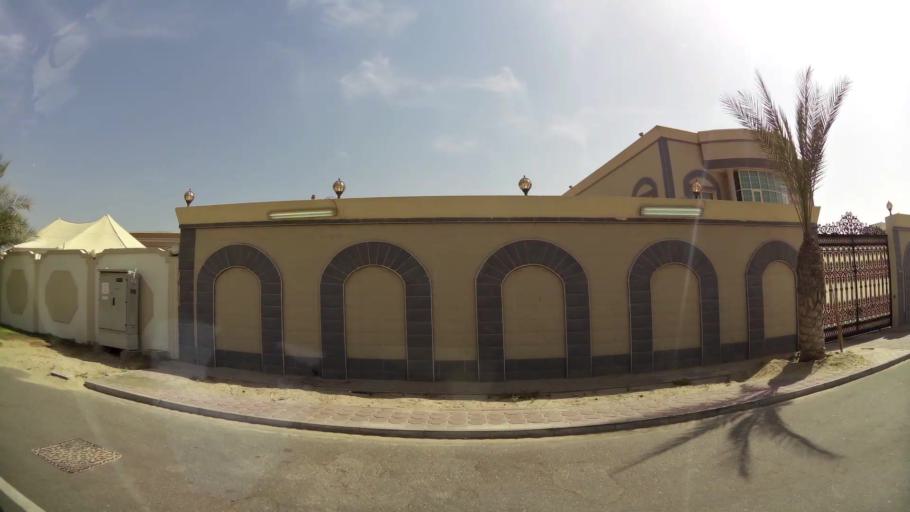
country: AE
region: Ash Shariqah
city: Sharjah
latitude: 25.2005
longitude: 55.4032
